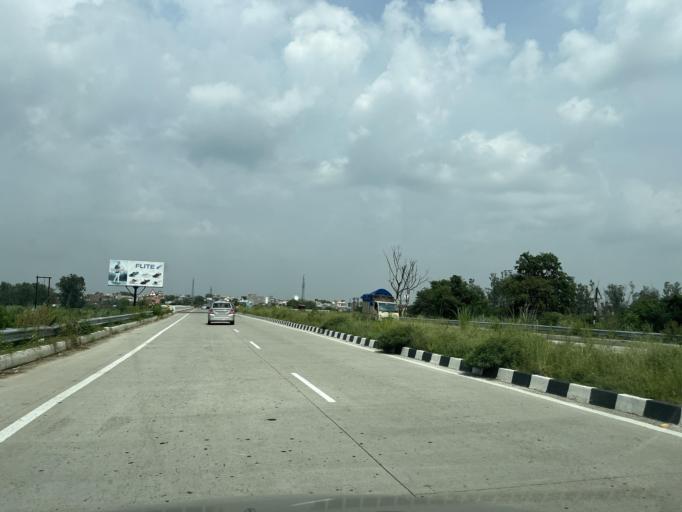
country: IN
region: Uttar Pradesh
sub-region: Bijnor
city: Sherkot
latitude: 29.3246
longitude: 78.5644
